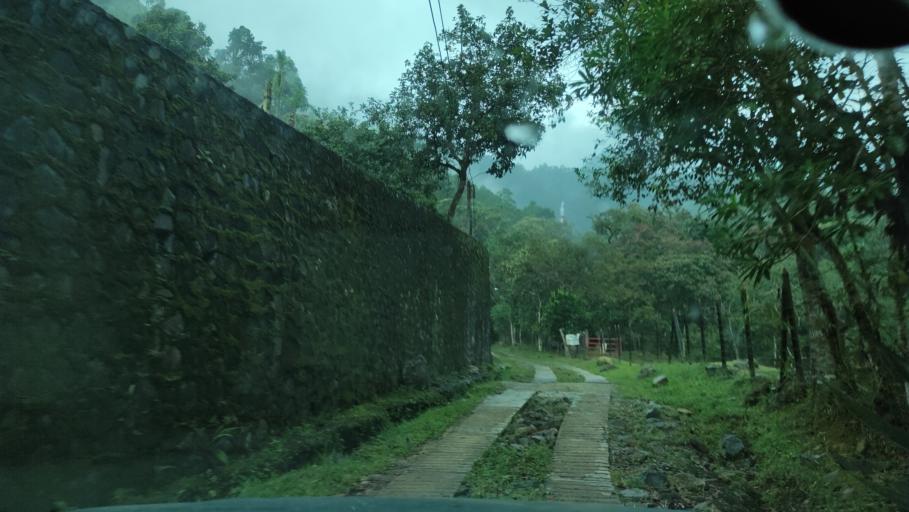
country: CO
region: Valle del Cauca
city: Jamundi
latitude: 3.3197
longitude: -76.6341
